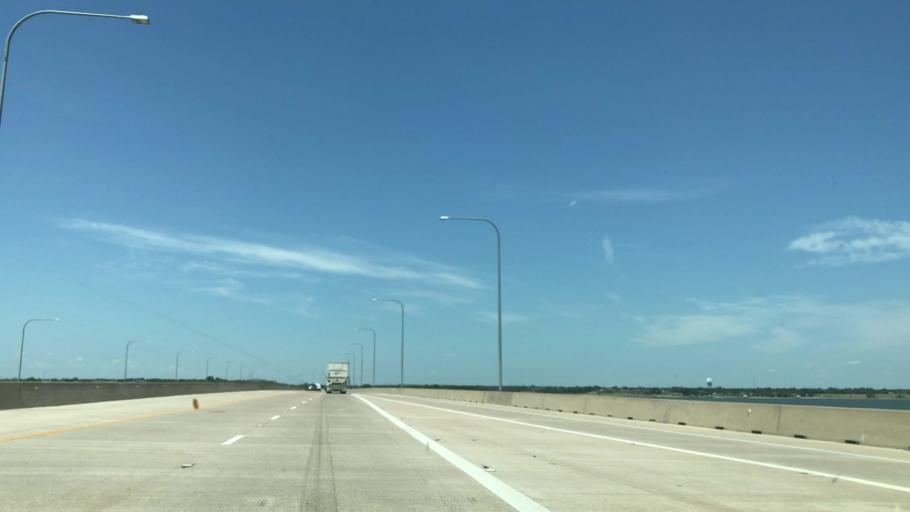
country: US
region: Texas
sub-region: Dallas County
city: Rowlett
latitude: 32.8654
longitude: -96.5539
